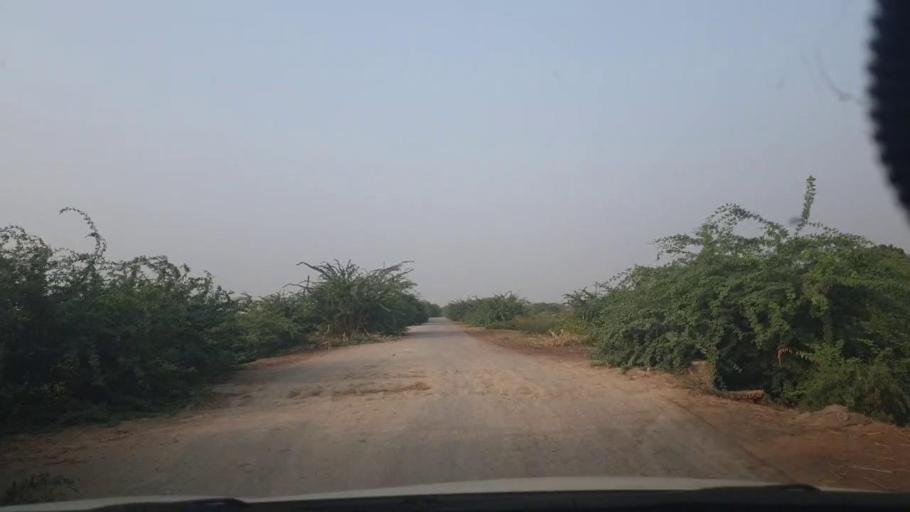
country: PK
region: Sindh
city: Bulri
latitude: 24.8306
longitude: 68.4029
